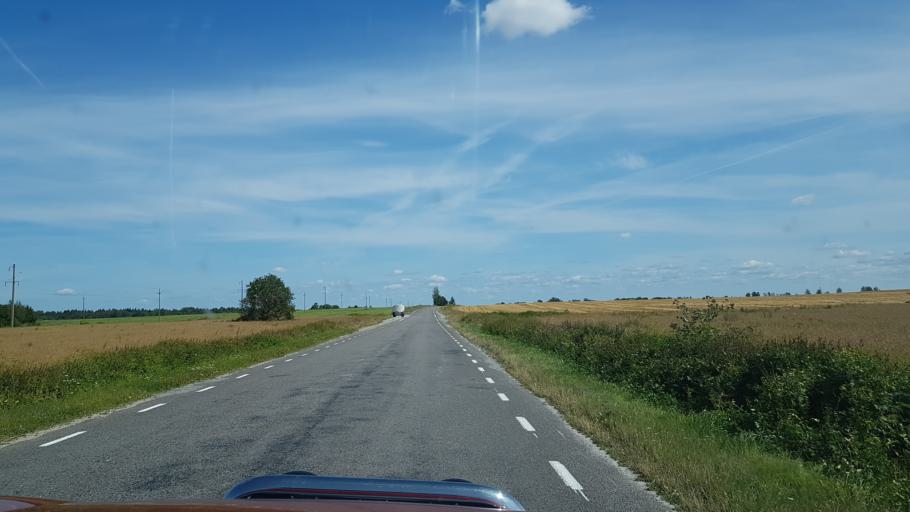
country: EE
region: Jaervamaa
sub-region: Jaerva-Jaani vald
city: Jarva-Jaani
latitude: 59.0427
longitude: 25.9737
